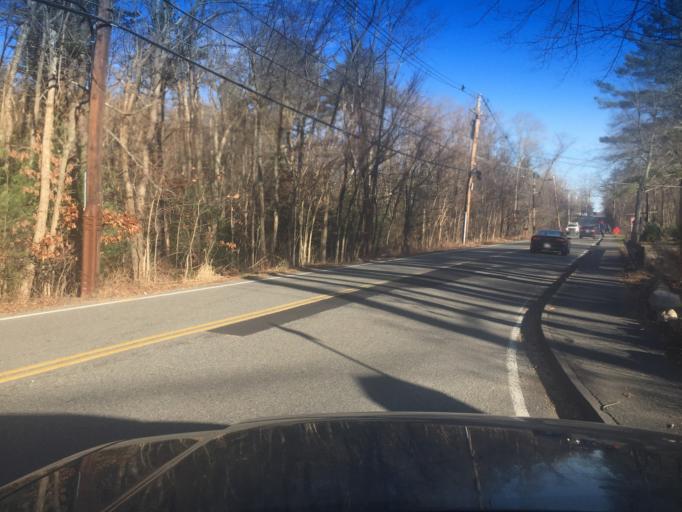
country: US
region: Massachusetts
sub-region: Middlesex County
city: Holliston
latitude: 42.2037
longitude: -71.4602
